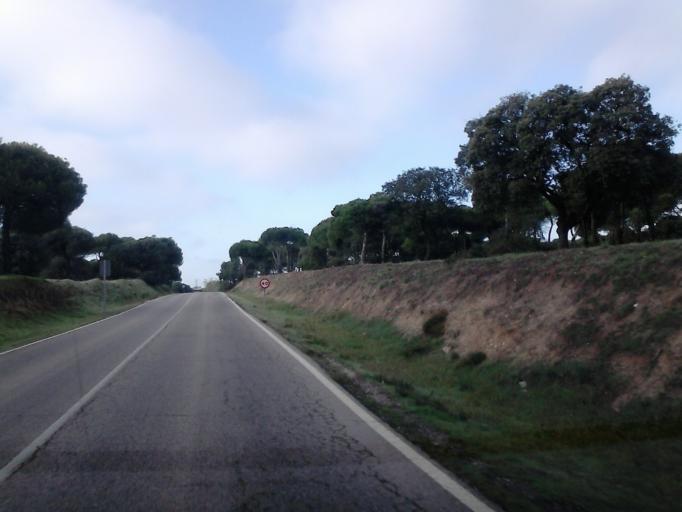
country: ES
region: Madrid
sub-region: Provincia de Madrid
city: Las Rozas de Madrid
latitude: 40.5132
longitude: -3.8871
